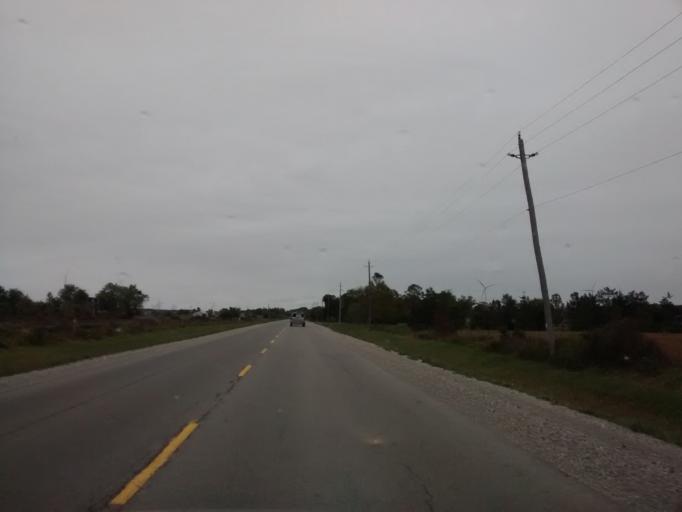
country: CA
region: Ontario
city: Hamilton
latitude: 42.8672
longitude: -79.7444
